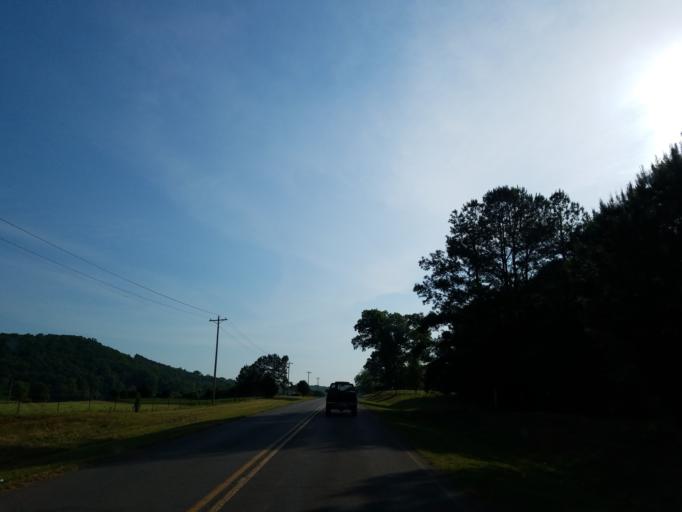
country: US
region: Georgia
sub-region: Chattooga County
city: Trion
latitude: 34.5674
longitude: -85.1660
